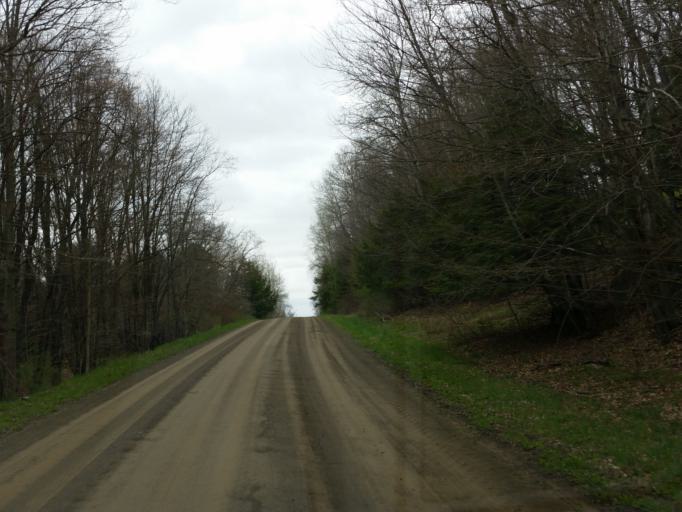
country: US
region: New York
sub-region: Allegany County
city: Andover
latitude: 42.0447
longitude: -77.7307
